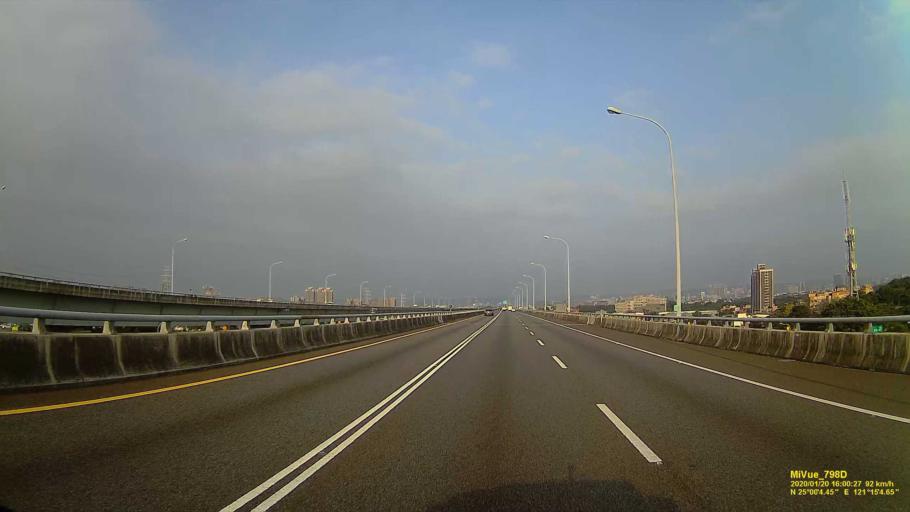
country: TW
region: Taiwan
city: Taoyuan City
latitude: 25.0049
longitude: 121.2506
